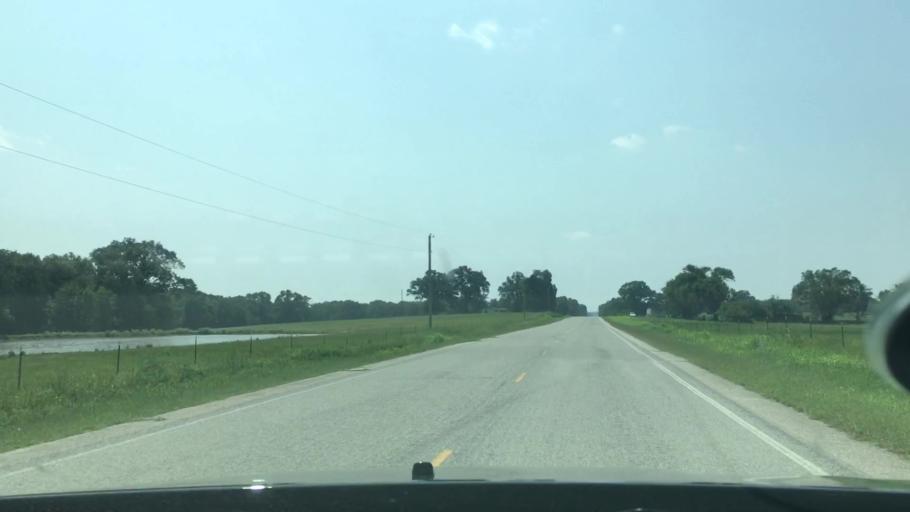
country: US
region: Oklahoma
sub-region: Atoka County
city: Atoka
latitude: 34.2755
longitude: -95.9361
